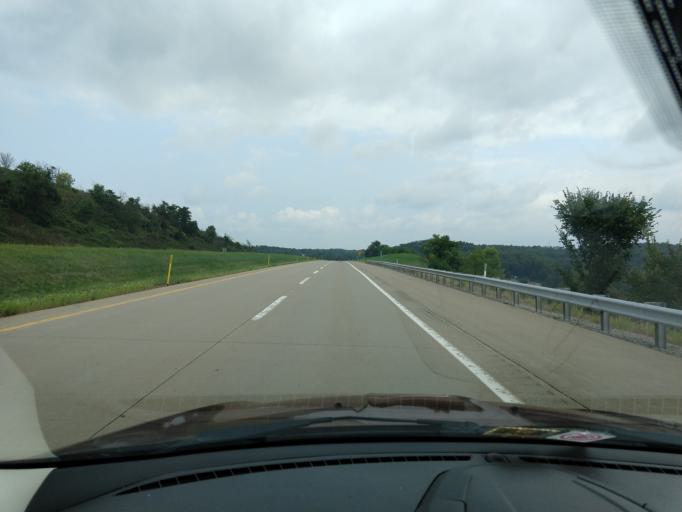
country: US
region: Pennsylvania
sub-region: Washington County
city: Gastonville
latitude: 40.2358
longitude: -79.9819
